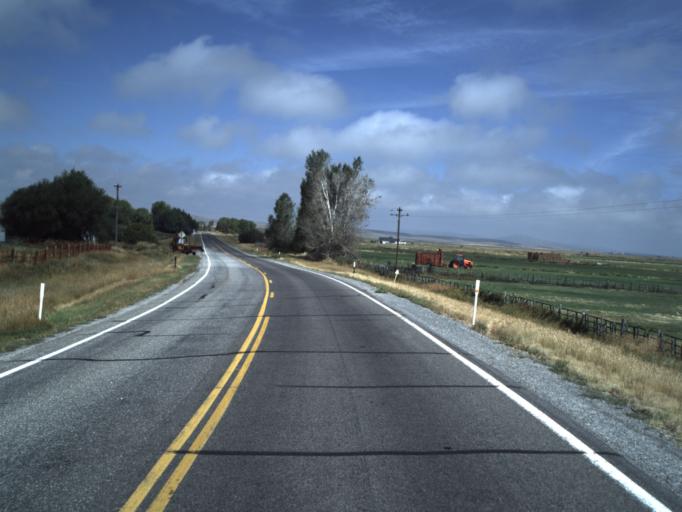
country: US
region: Utah
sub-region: Rich County
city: Randolph
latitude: 41.7056
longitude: -111.1593
